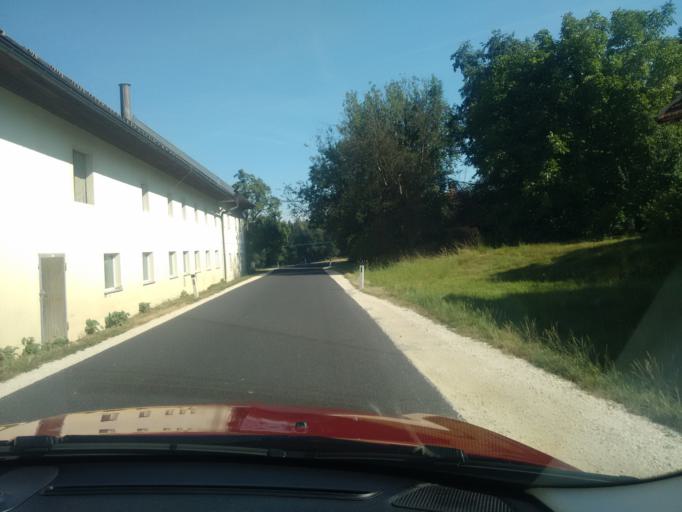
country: AT
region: Upper Austria
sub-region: Wels-Land
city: Sattledt
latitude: 48.0815
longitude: 14.0713
